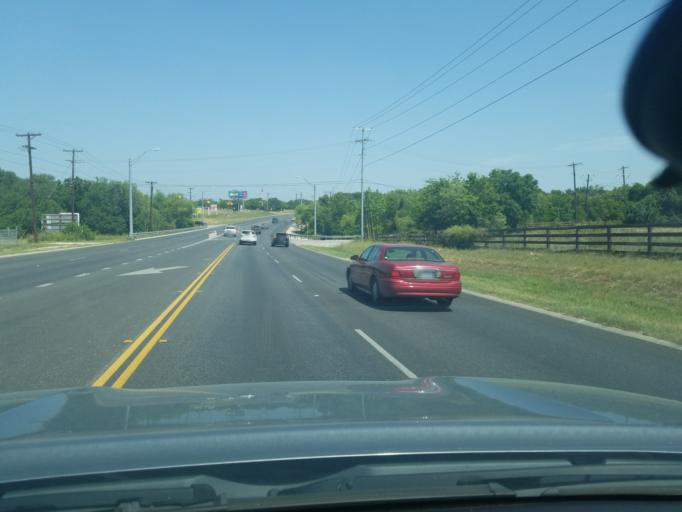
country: US
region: Texas
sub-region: Guadalupe County
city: Lake Dunlap
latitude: 29.6893
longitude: -98.0716
